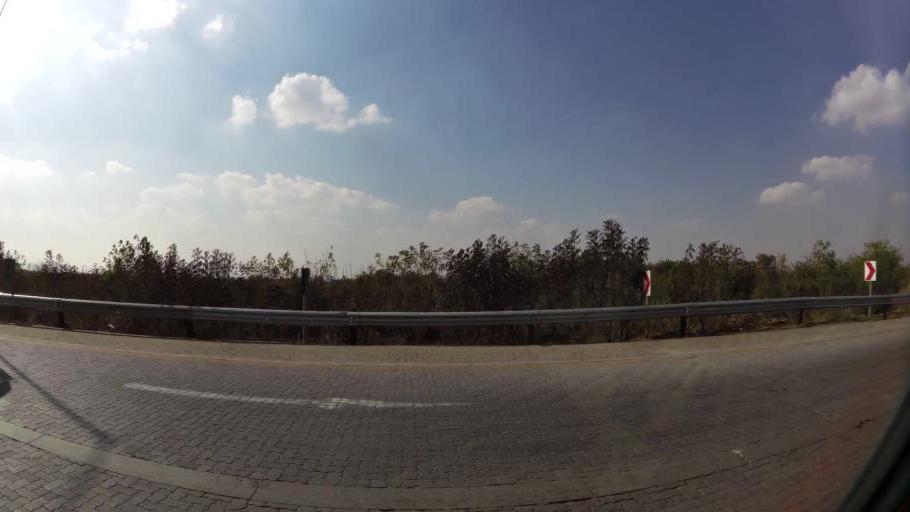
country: ZA
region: North-West
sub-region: Bojanala Platinum District Municipality
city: Rustenburg
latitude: -25.5603
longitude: 27.1447
